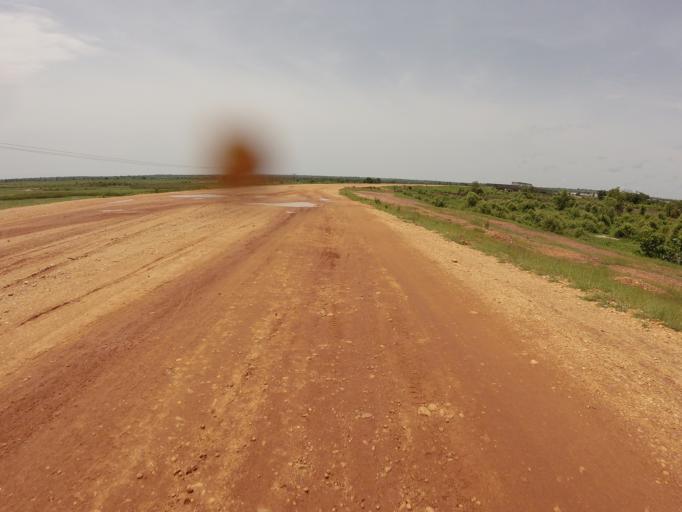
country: GH
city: Kpandae
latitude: 8.7048
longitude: 0.1655
